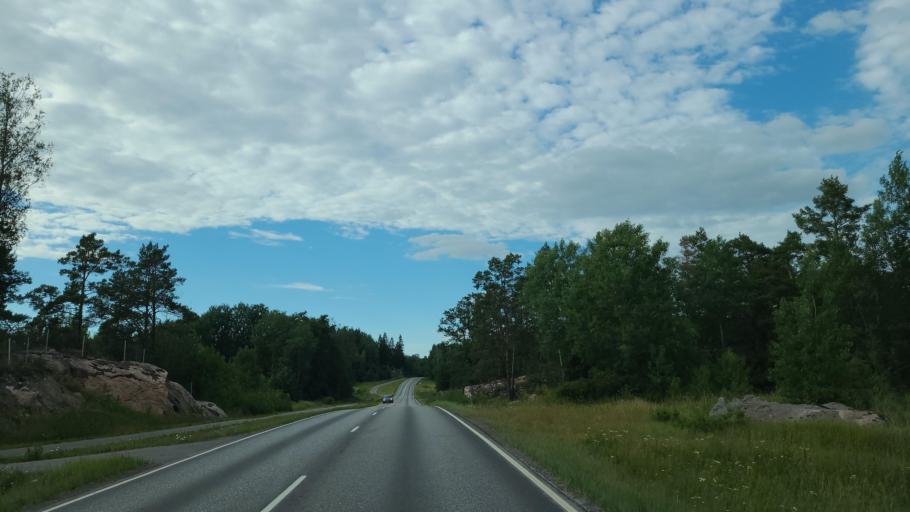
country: FI
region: Varsinais-Suomi
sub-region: Turku
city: Rymaettylae
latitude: 60.4038
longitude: 21.8958
